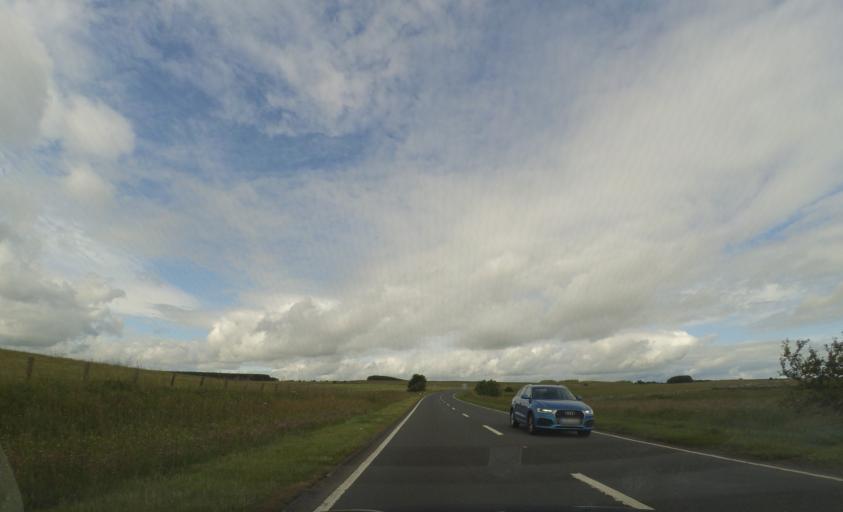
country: GB
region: Scotland
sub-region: The Scottish Borders
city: Hawick
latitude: 55.4613
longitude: -2.7815
